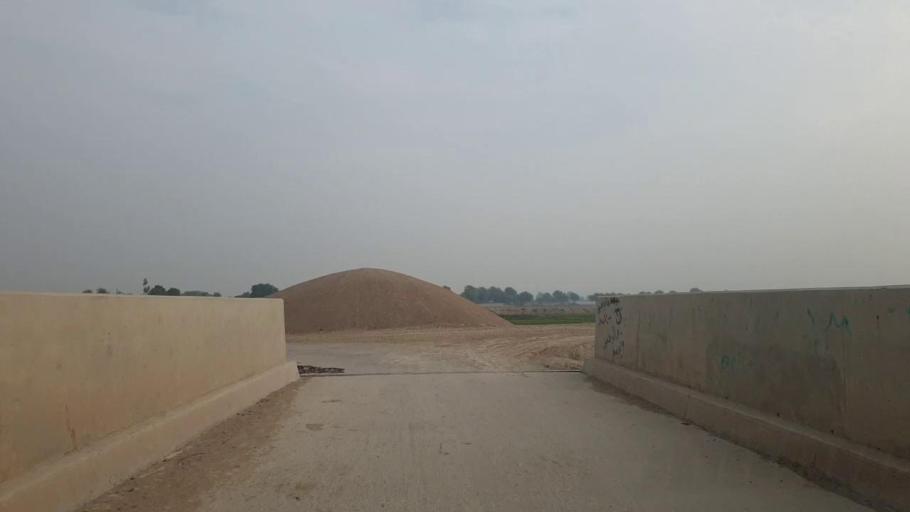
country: PK
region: Sindh
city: Sann
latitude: 25.9741
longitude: 68.1885
